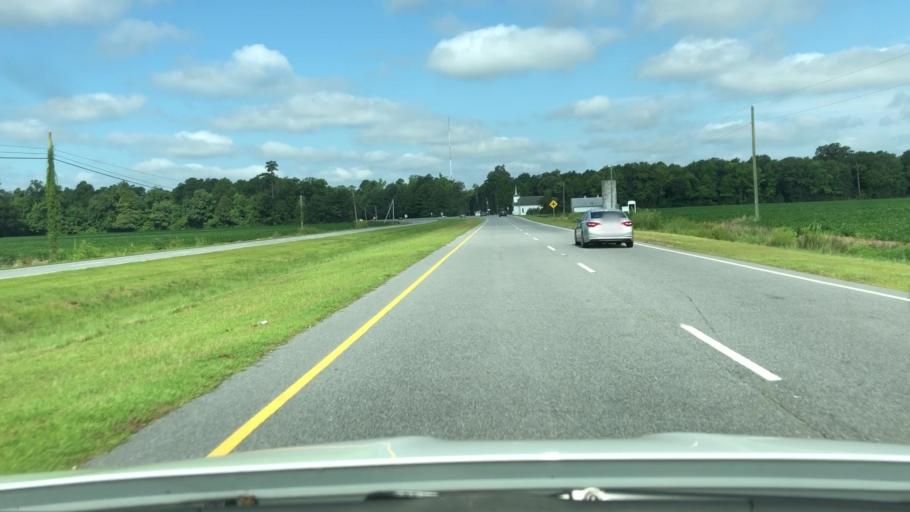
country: US
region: North Carolina
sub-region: Perquimans County
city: Hertford
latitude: 36.2120
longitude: -76.4269
